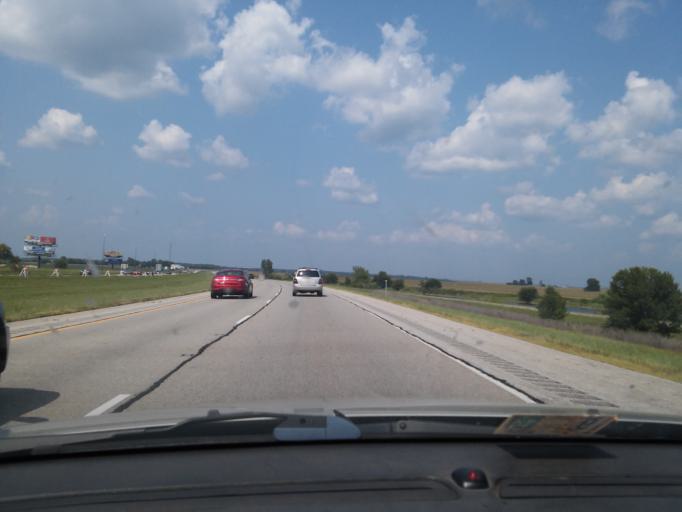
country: US
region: Illinois
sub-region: Logan County
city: Atlanta
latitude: 40.3129
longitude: -89.1616
